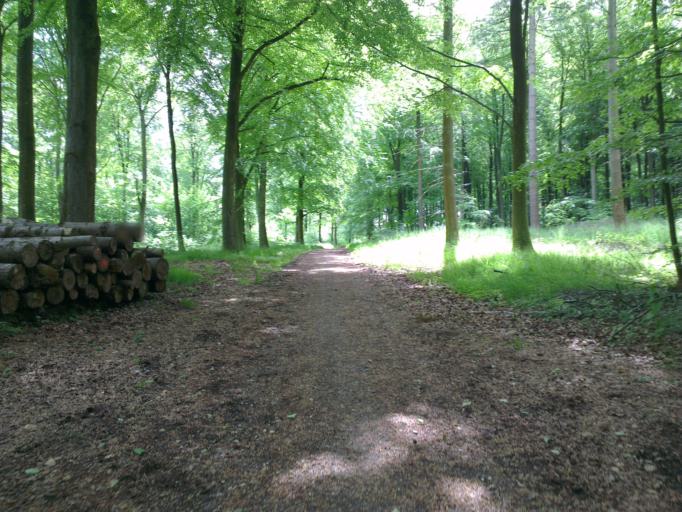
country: DK
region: Capital Region
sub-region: Frederikssund Kommune
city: Frederikssund
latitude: 55.8443
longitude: 12.0231
